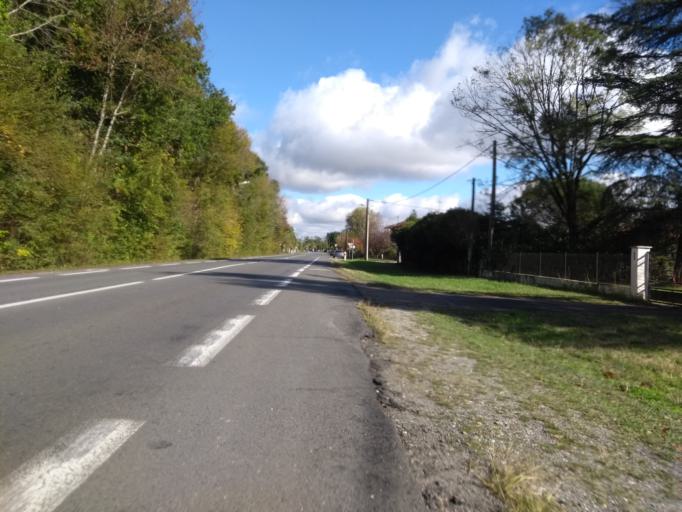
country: FR
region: Aquitaine
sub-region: Departement de la Gironde
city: Saint-Aubin-de-Medoc
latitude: 44.7763
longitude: -0.7026
